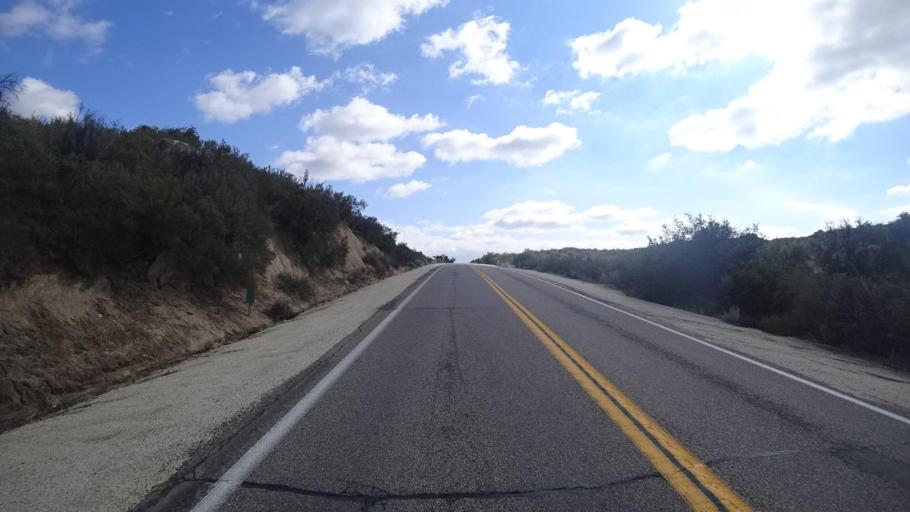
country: US
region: California
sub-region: San Diego County
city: Campo
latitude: 32.6965
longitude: -116.4897
